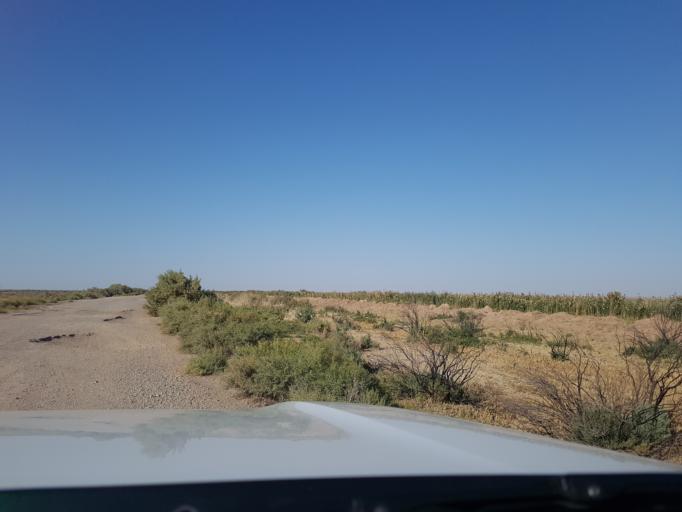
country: IR
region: Razavi Khorasan
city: Sarakhs
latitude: 36.9444
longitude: 61.3787
